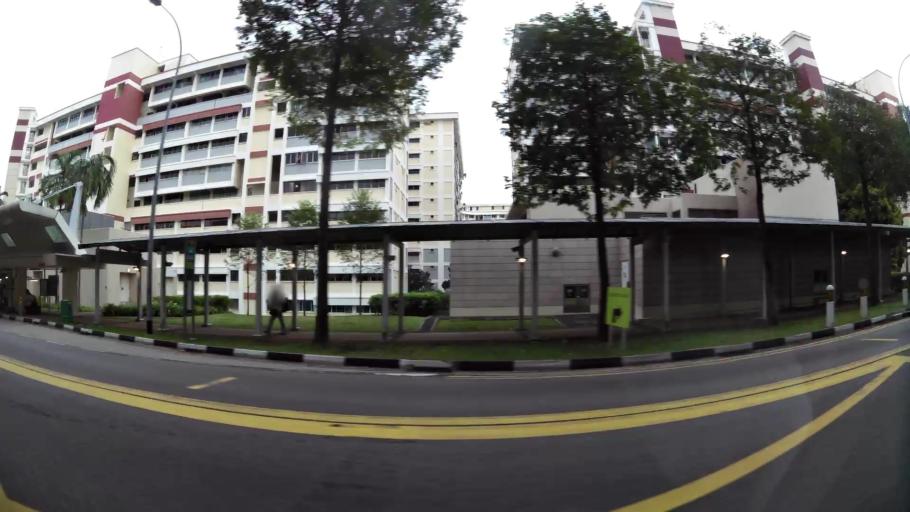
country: SG
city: Singapore
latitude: 1.3498
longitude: 103.8740
